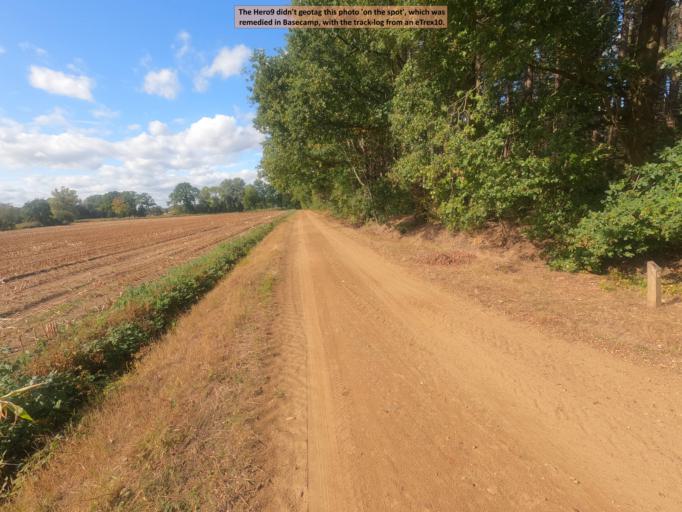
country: BE
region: Flanders
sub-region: Provincie Antwerpen
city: Lille
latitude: 51.2579
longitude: 4.8423
